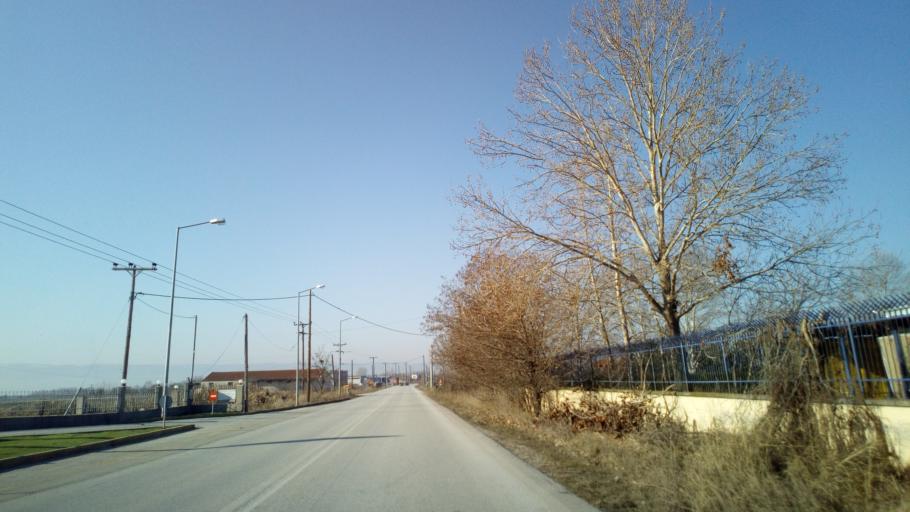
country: GR
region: Central Macedonia
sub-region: Nomos Thessalonikis
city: Kolchikon
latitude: 40.7530
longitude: 23.1121
